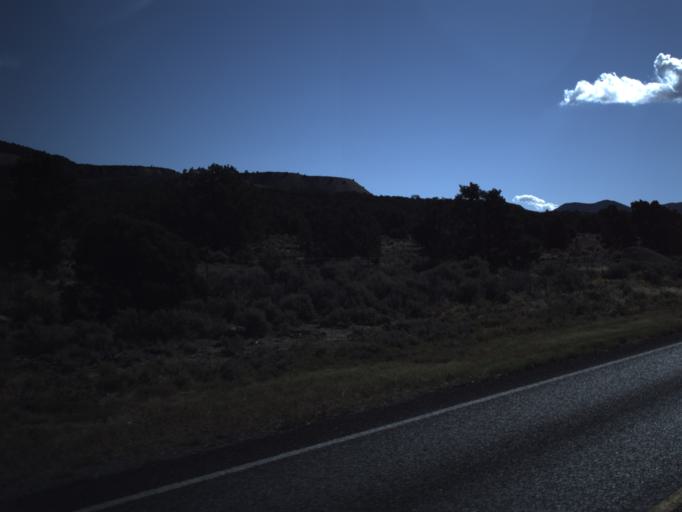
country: US
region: Utah
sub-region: Washington County
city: Enterprise
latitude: 37.6205
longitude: -113.4147
